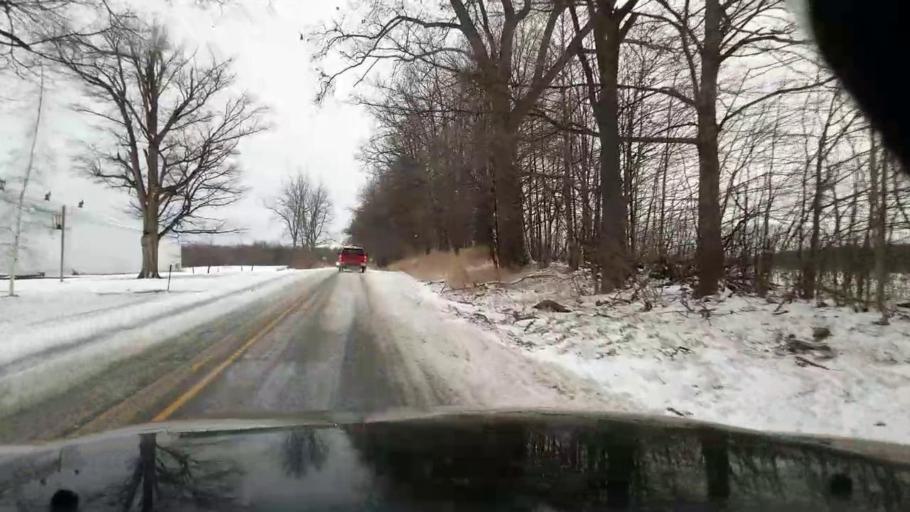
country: US
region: Michigan
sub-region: Jackson County
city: Spring Arbor
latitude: 42.1451
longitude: -84.4990
